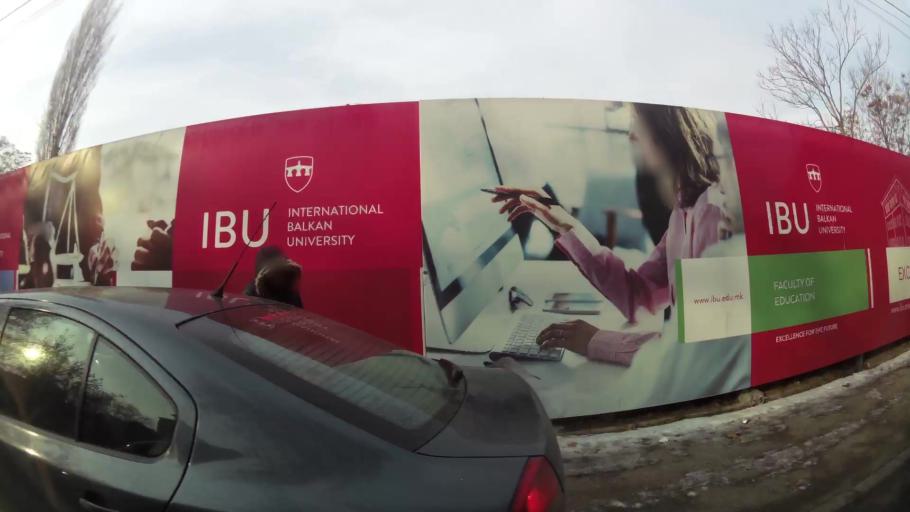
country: MK
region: Cair
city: Cair
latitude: 42.0161
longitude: 21.4311
